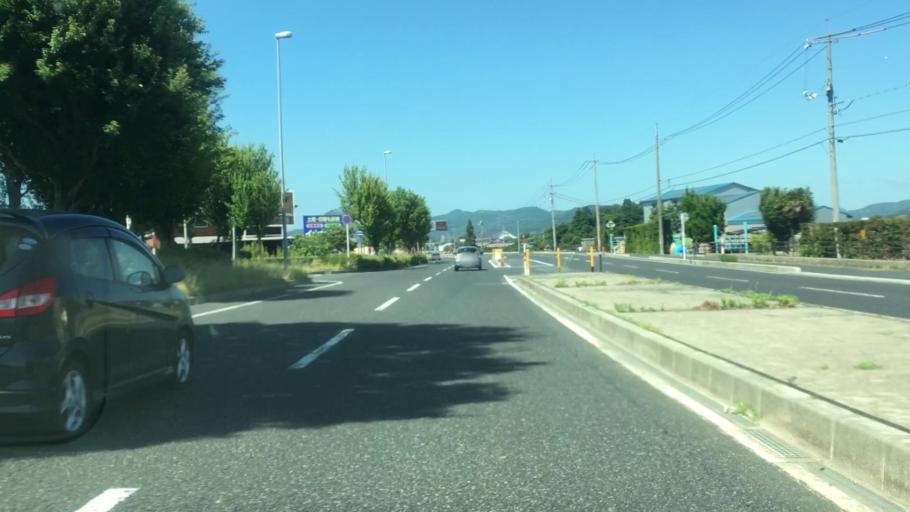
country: JP
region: Tottori
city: Tottori
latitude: 35.4680
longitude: 134.2156
